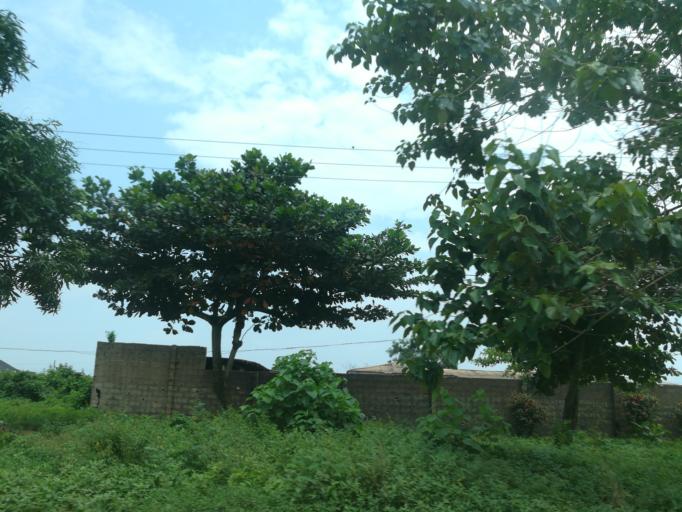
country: NG
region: Lagos
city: Ikorodu
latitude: 6.5916
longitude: 3.5883
